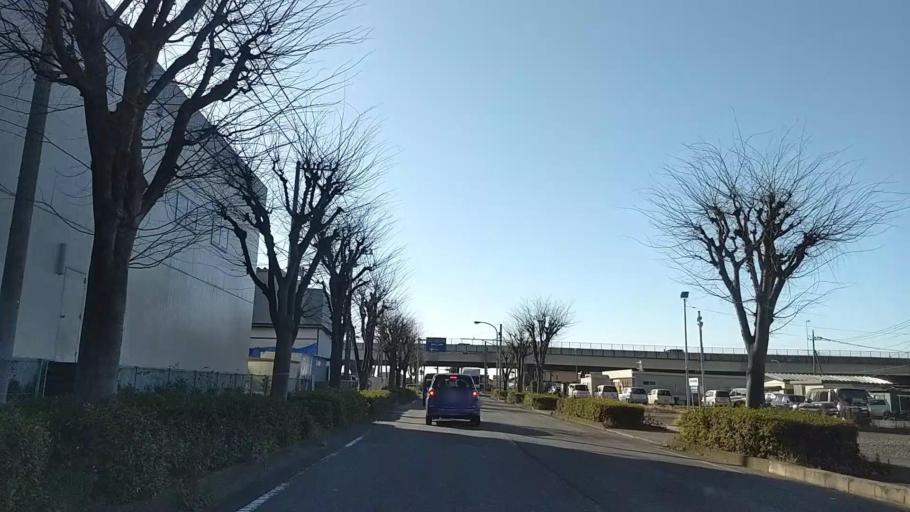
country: JP
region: Kanagawa
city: Atsugi
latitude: 35.4204
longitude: 139.3554
